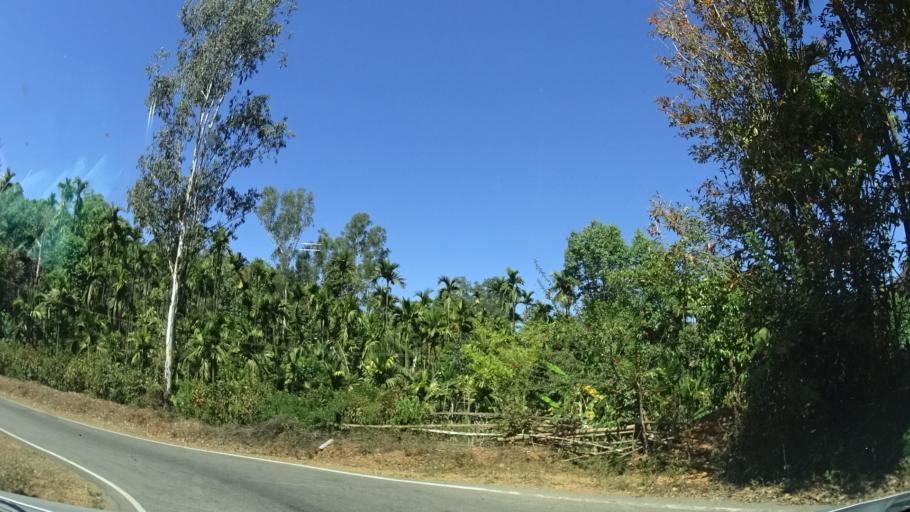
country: IN
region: Karnataka
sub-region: Chikmagalur
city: Sringeri
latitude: 13.2048
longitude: 75.2850
